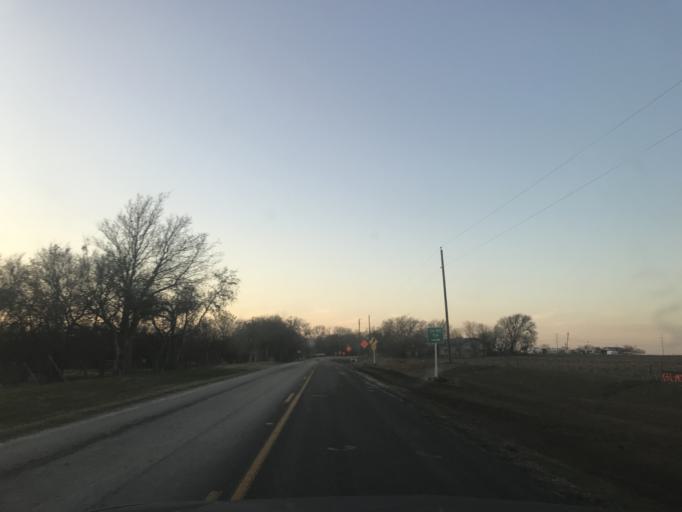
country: US
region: Texas
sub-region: Williamson County
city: Hutto
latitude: 30.5039
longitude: -97.5183
